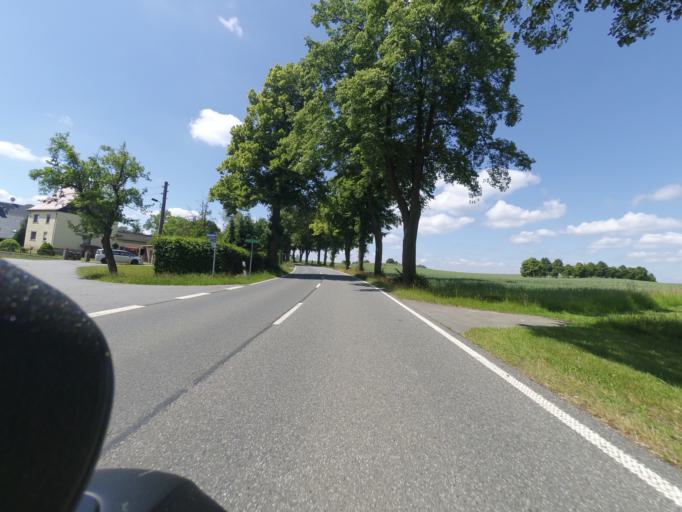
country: DE
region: Saxony
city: Sebnitz
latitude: 50.9457
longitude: 14.2360
